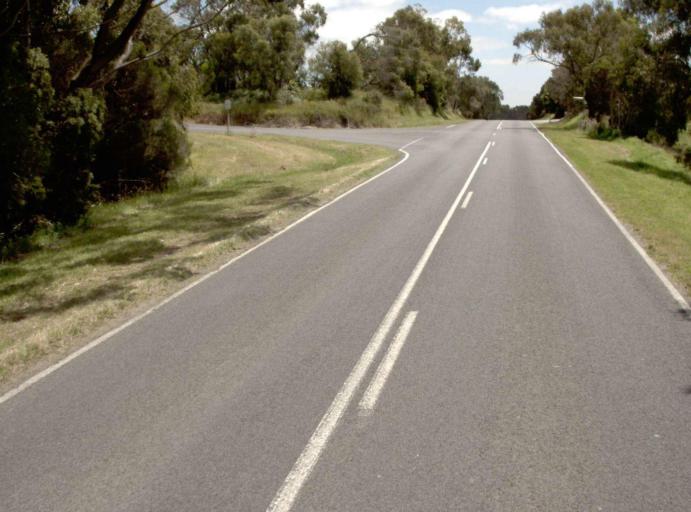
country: AU
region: Victoria
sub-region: Bass Coast
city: North Wonthaggi
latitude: -38.5851
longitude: 146.0223
